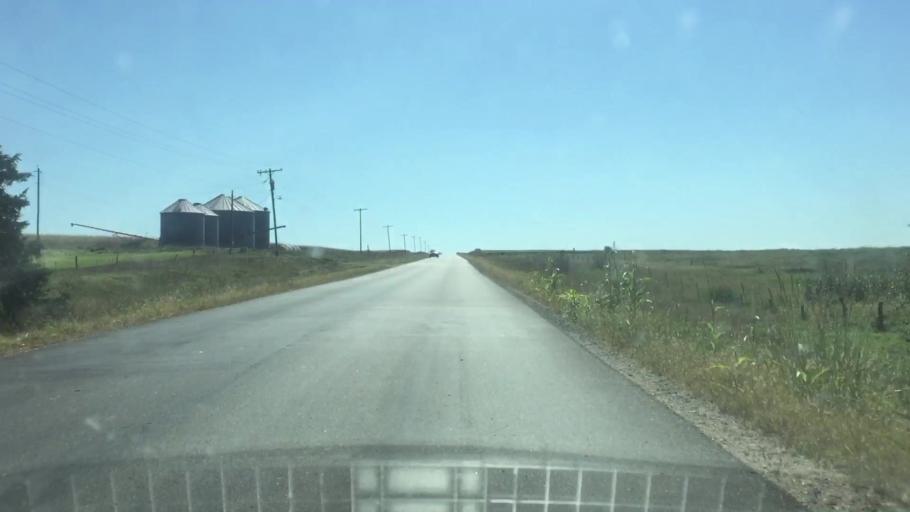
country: US
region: Kansas
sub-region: Marshall County
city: Marysville
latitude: 39.9268
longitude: -96.6009
